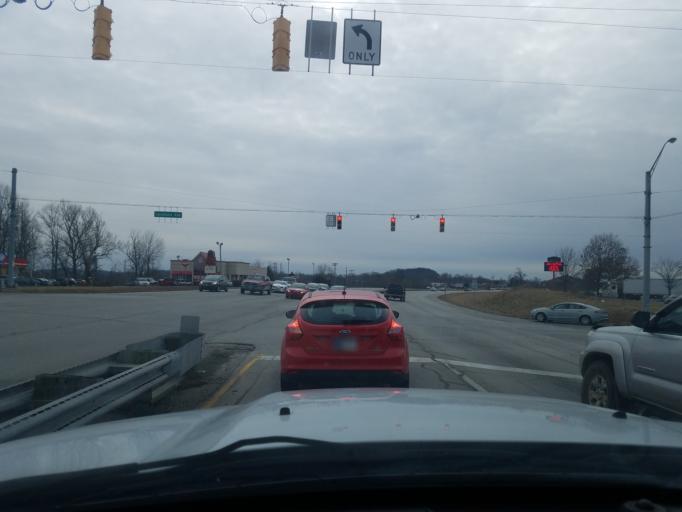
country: US
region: Indiana
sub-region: Harrison County
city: Corydon
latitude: 38.2355
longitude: -86.1276
